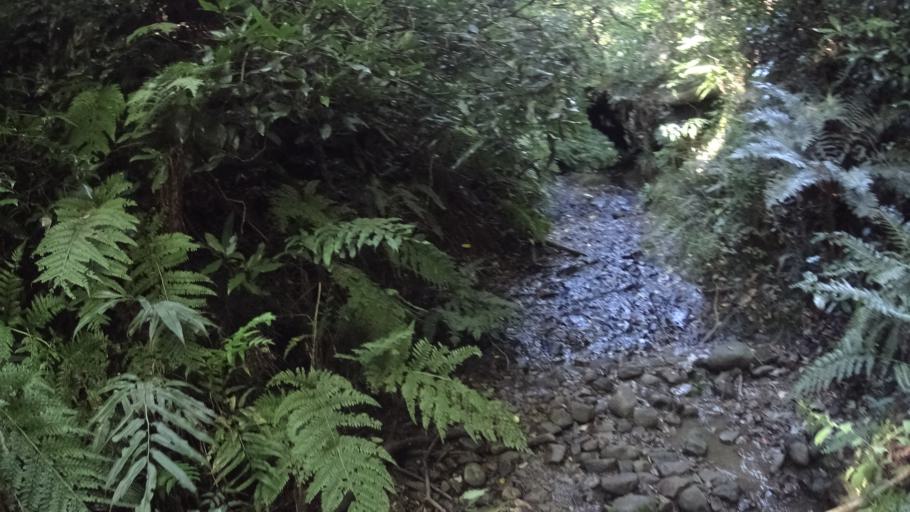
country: JP
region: Kanagawa
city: Hayama
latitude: 35.2824
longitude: 139.6087
